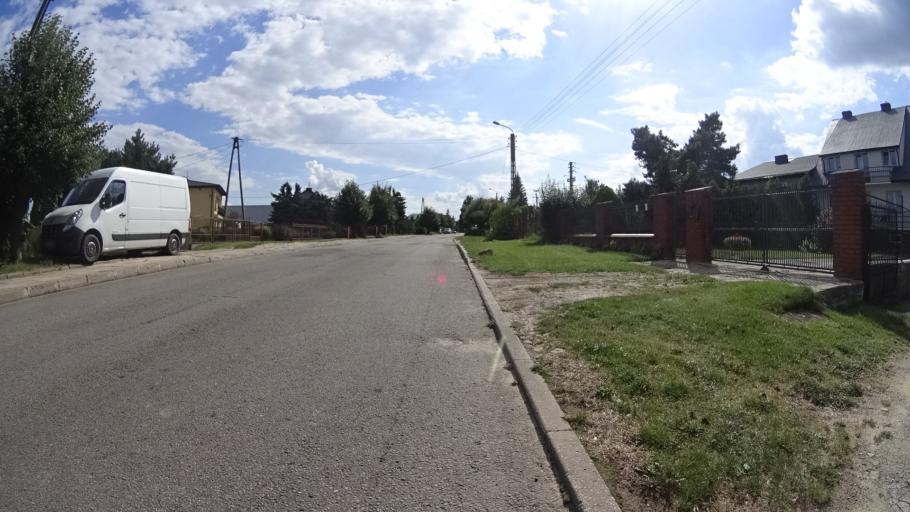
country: PL
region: Masovian Voivodeship
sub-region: Powiat grojecki
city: Mogielnica
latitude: 51.6872
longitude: 20.7190
